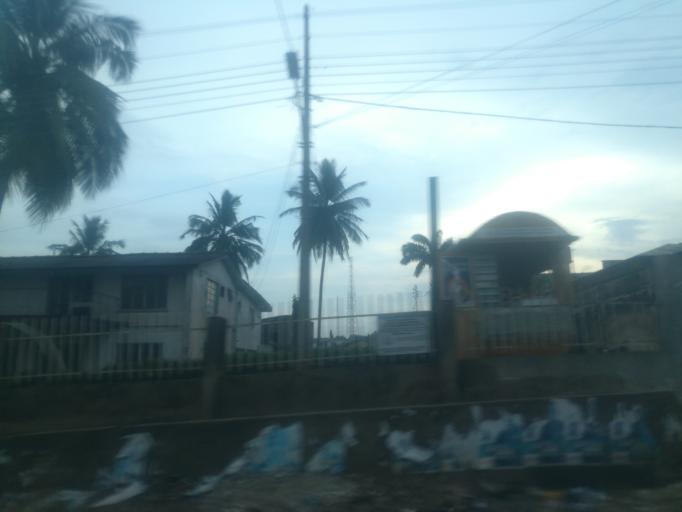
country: NG
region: Oyo
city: Ibadan
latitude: 7.4187
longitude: 3.8985
